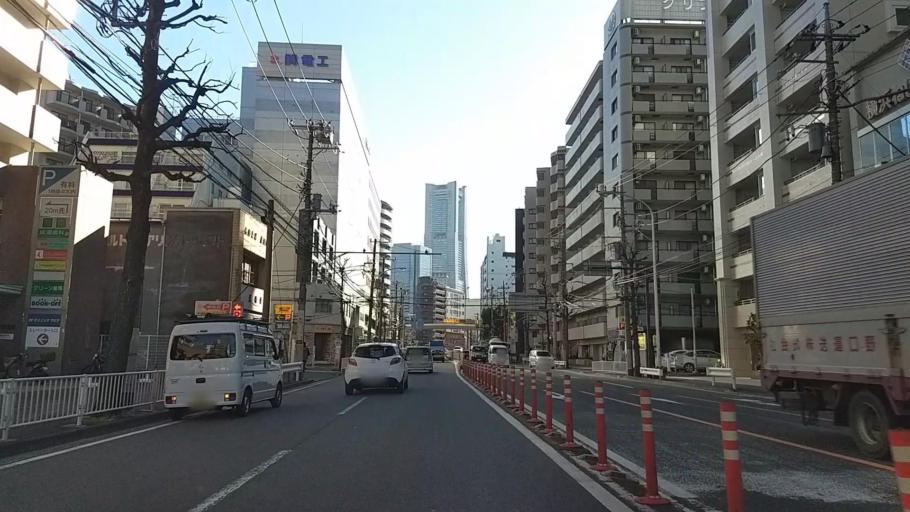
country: JP
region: Kanagawa
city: Yokohama
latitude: 35.4607
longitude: 139.6207
